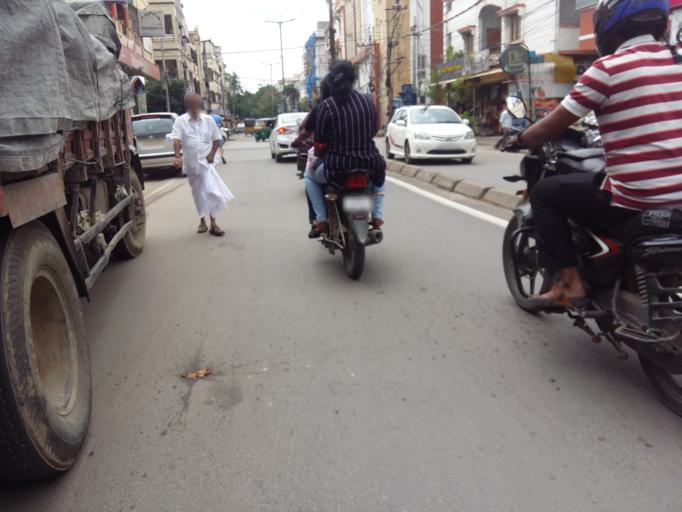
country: IN
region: Telangana
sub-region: Rangareddi
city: Kukatpalli
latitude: 17.4946
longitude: 78.4115
